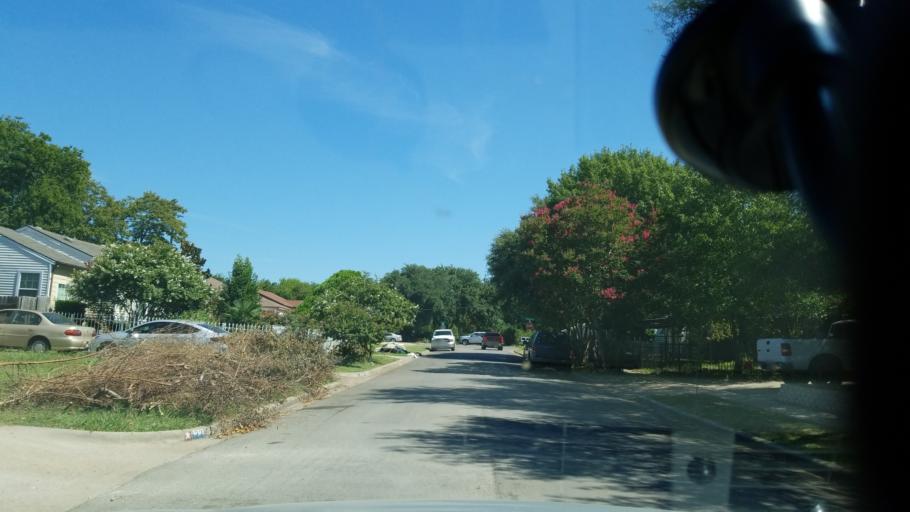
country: US
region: Texas
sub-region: Dallas County
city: Cockrell Hill
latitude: 32.7051
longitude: -96.8219
